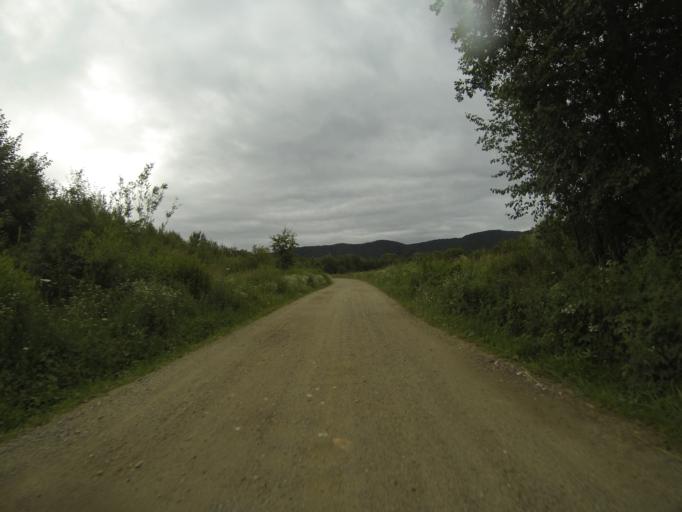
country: RO
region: Brasov
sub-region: Comuna Sinca Noua
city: Sinca Noua
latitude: 45.7274
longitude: 25.2233
